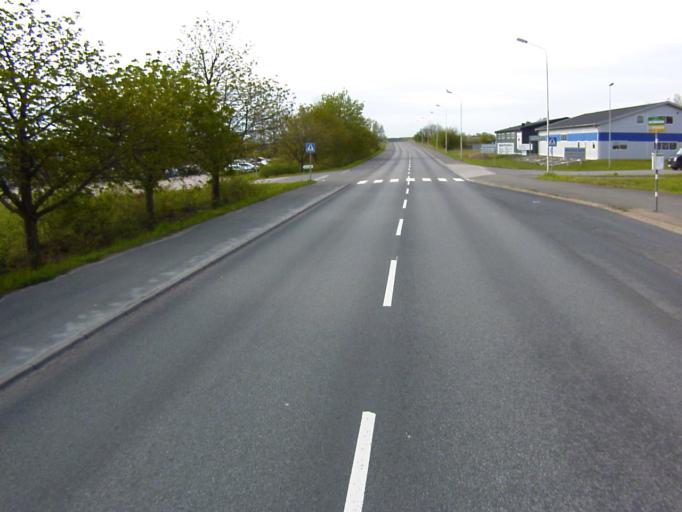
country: SE
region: Skane
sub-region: Kristianstads Kommun
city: Kristianstad
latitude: 56.0197
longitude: 14.1243
